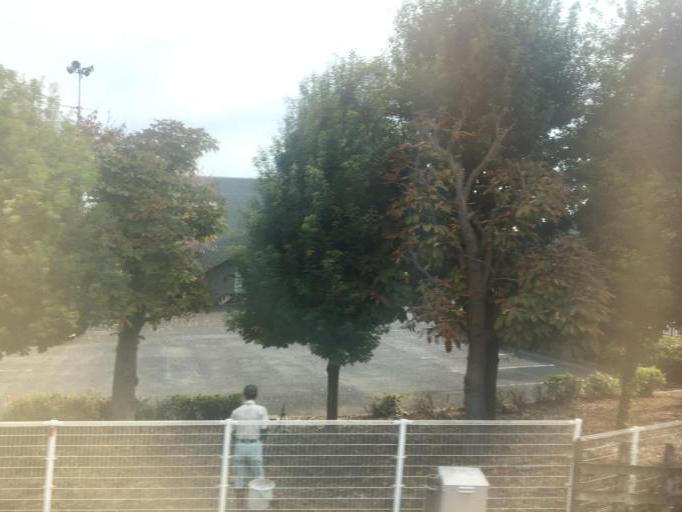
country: JP
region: Saitama
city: Sayama
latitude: 35.8166
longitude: 139.4137
